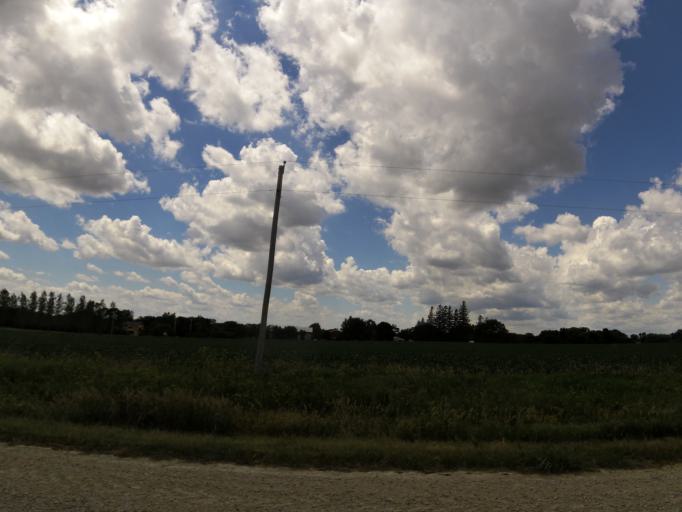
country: US
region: Iowa
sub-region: Fayette County
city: Oelwein
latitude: 42.6367
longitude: -91.9087
